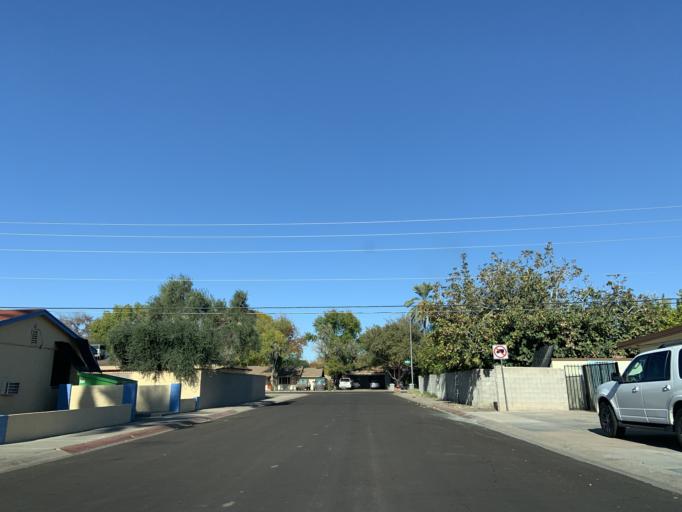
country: US
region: Arizona
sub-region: Maricopa County
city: Mesa
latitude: 33.4155
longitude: -111.8598
